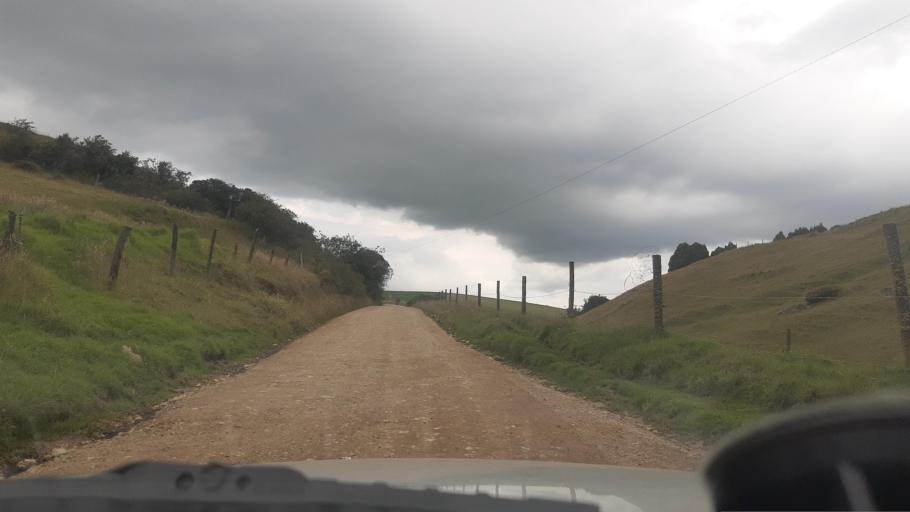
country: CO
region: Cundinamarca
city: Suesca
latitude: 5.1377
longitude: -73.7904
